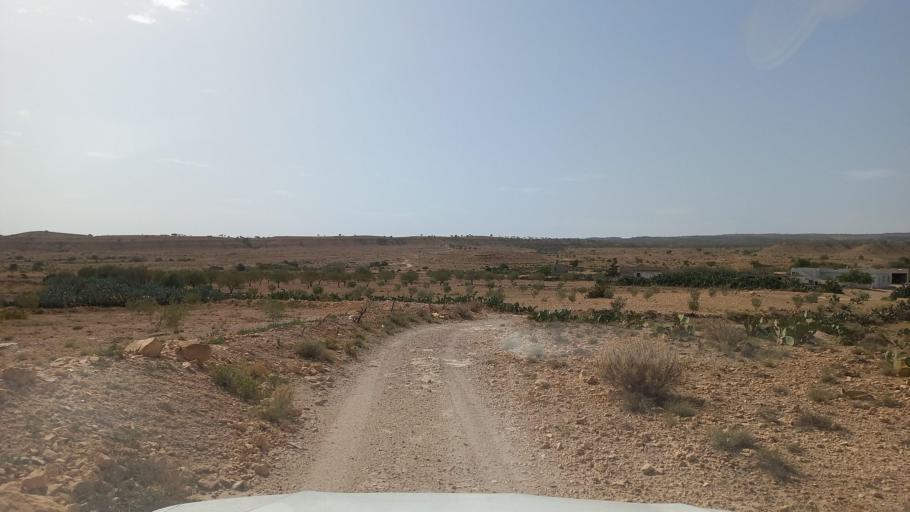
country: TN
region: Al Qasrayn
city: Kasserine
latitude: 35.3011
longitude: 8.9396
